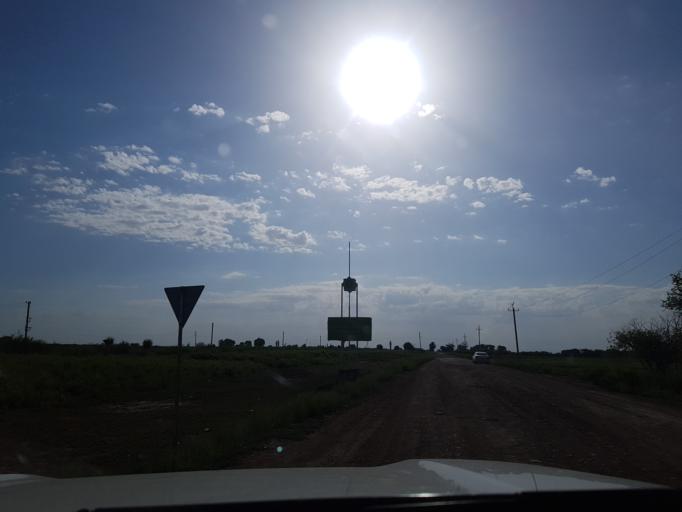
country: TM
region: Dasoguz
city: Koeneuergench
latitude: 41.8791
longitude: 58.7065
